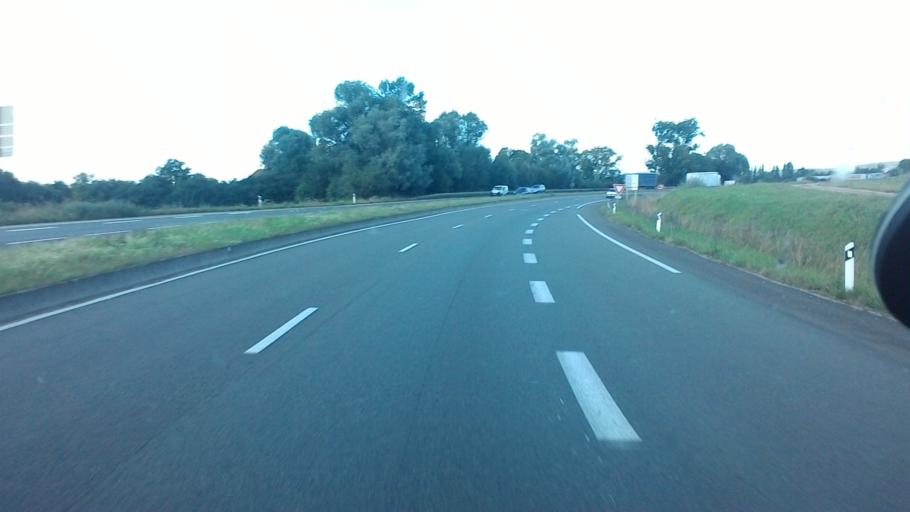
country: FR
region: Franche-Comte
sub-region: Departement de la Haute-Saone
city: Pusey
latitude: 47.6371
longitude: 6.1357
